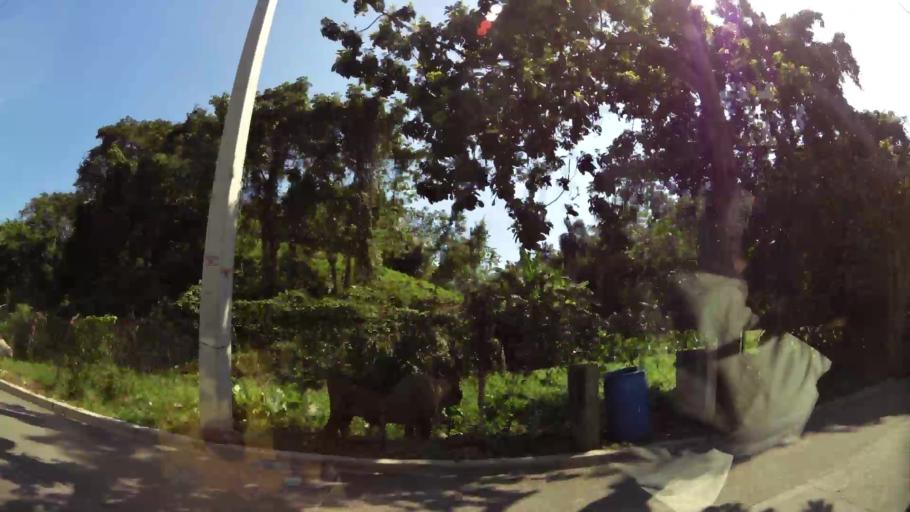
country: DO
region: Santo Domingo
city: Santo Domingo Oeste
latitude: 18.4740
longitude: -70.0032
